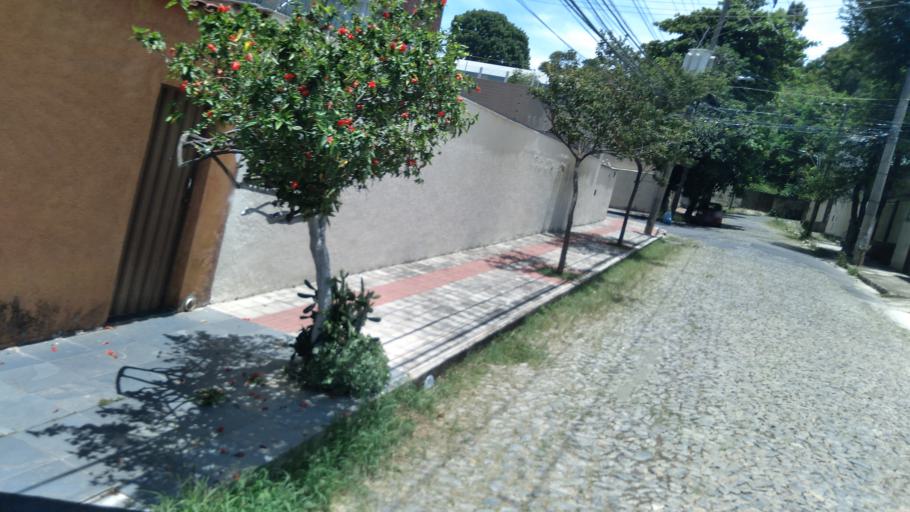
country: BR
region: Minas Gerais
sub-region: Belo Horizonte
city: Belo Horizonte
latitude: -19.9186
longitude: -43.9888
